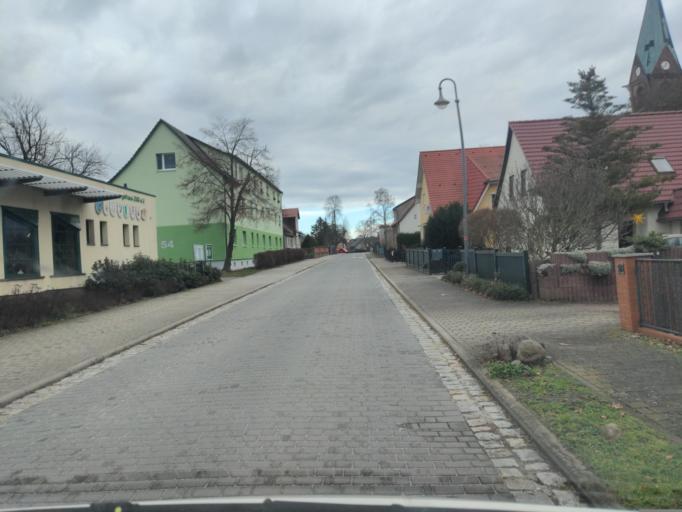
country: DE
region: Brandenburg
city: Cottbus
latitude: 51.7137
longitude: 14.3229
